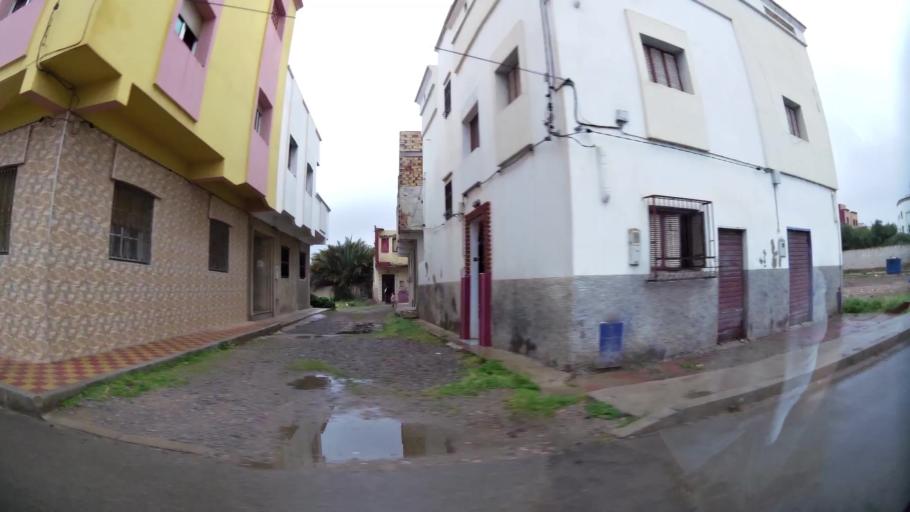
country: MA
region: Oriental
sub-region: Nador
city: Nador
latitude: 35.1646
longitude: -2.9540
